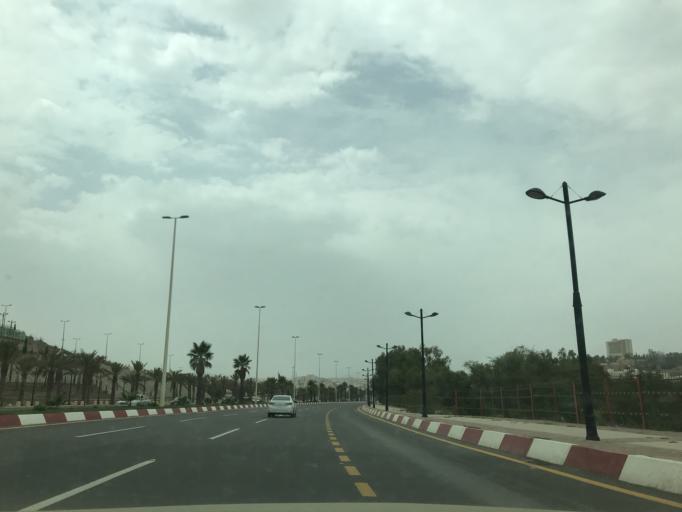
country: SA
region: Mintaqat al Bahah
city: Al Bahah
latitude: 19.8447
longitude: 41.5862
